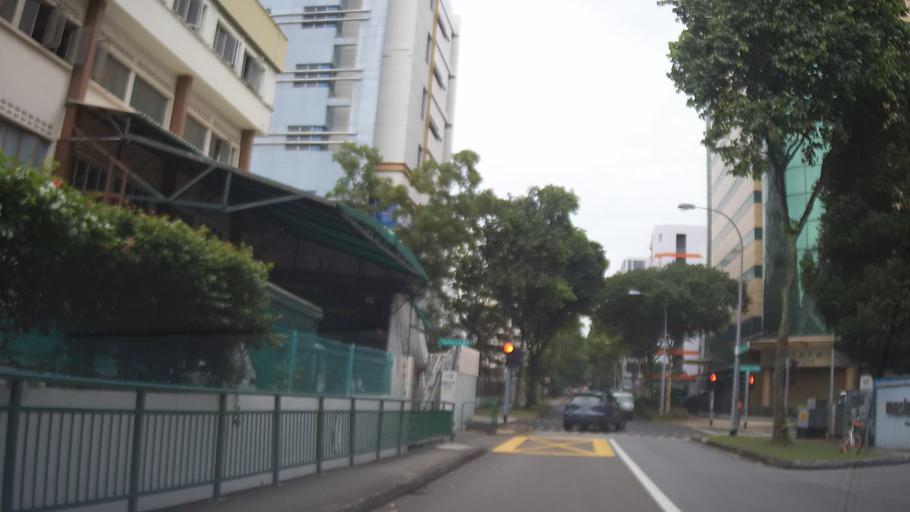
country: SG
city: Singapore
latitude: 1.3300
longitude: 103.8770
